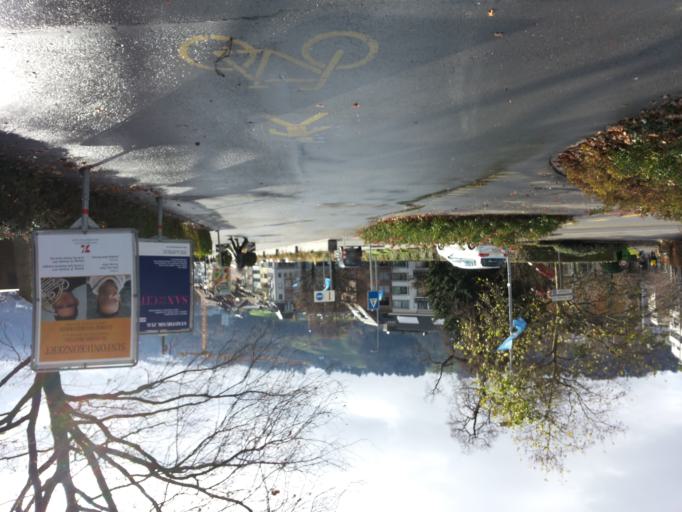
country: CH
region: Zug
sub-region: Zug
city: Zug
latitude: 47.1707
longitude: 8.5133
